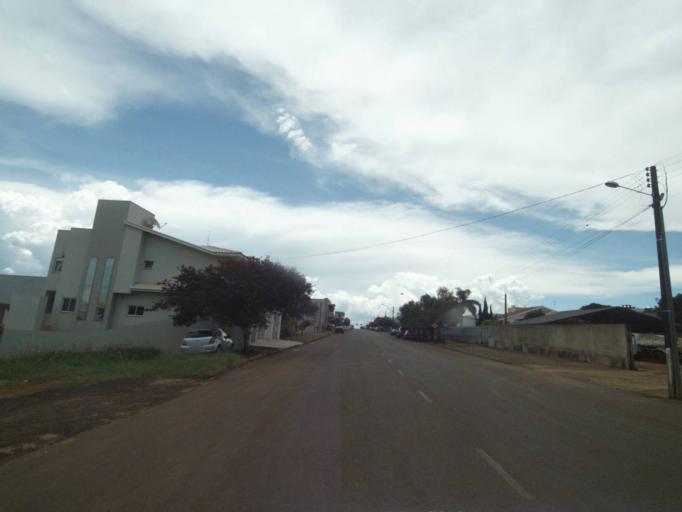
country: BR
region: Parana
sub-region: Guaraniacu
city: Guaraniacu
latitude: -25.1028
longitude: -52.8636
